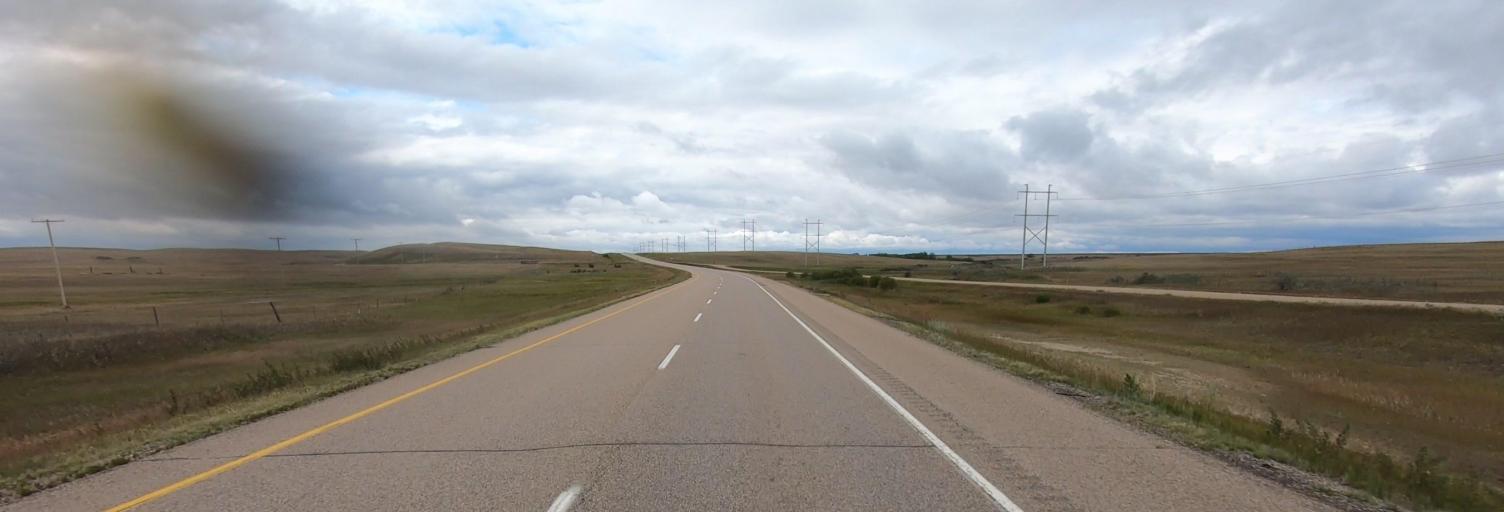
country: CA
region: Saskatchewan
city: Gravelbourg
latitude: 50.4801
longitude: -106.7997
